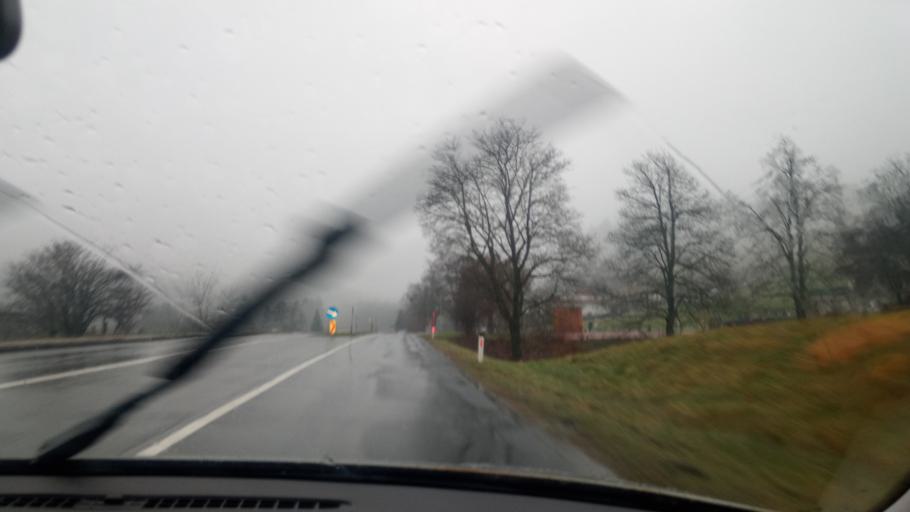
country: AT
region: Carinthia
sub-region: Politischer Bezirk Klagenfurt Land
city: Keutschach am See
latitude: 46.5902
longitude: 14.1737
